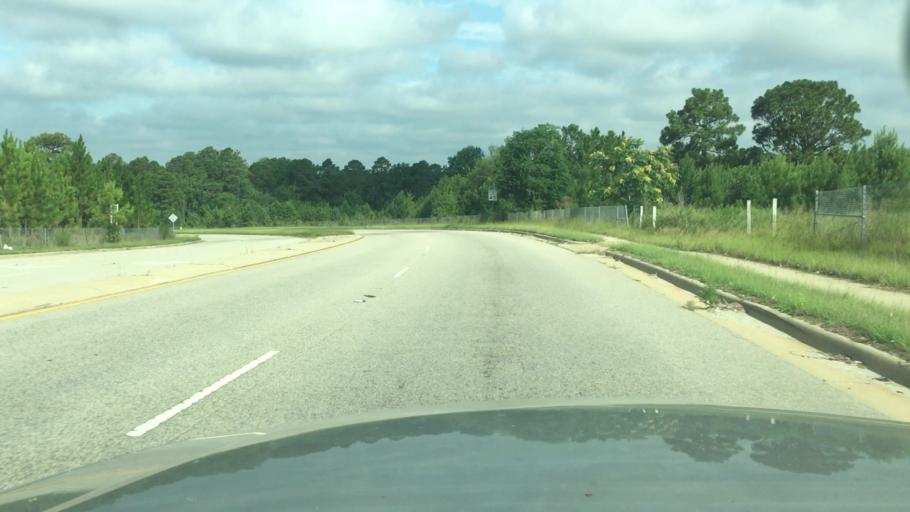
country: US
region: North Carolina
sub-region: Cumberland County
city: Hope Mills
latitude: 34.9916
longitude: -78.9497
